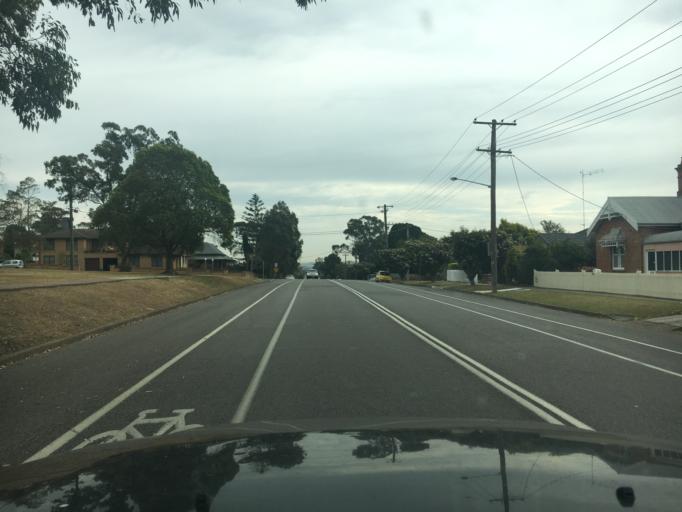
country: AU
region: New South Wales
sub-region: Maitland Municipality
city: East Maitland
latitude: -32.7544
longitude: 151.5927
